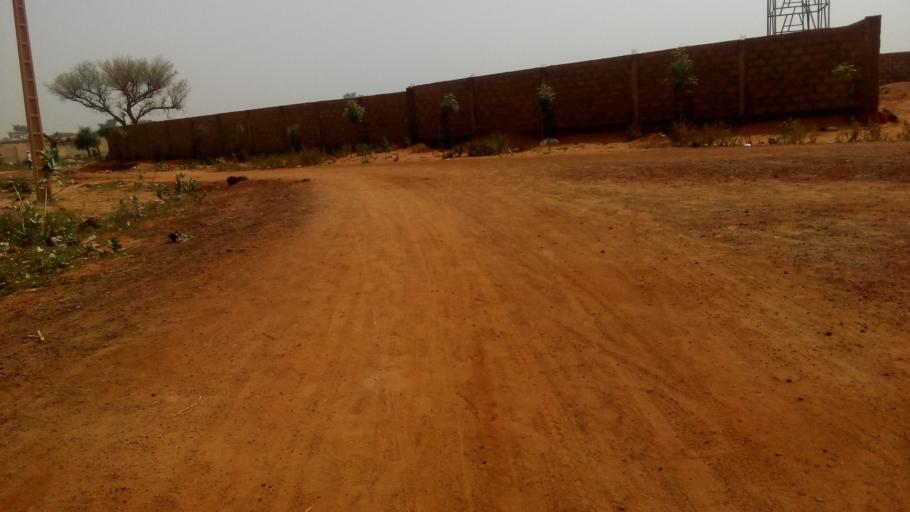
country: NE
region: Niamey
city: Niamey
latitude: 13.5419
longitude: 2.0596
